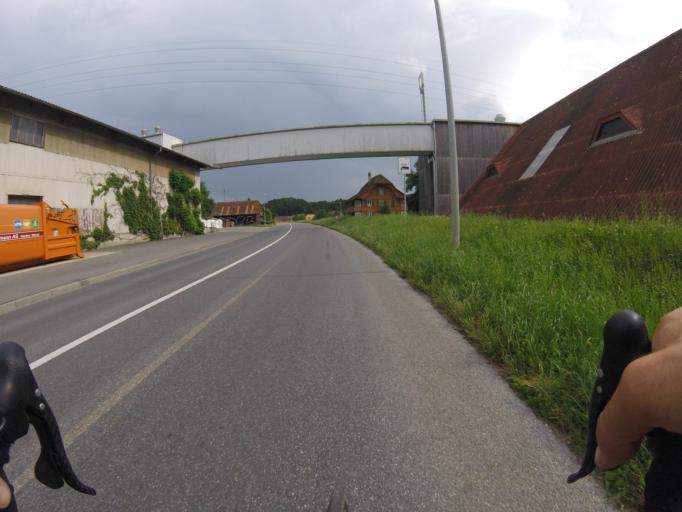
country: CH
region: Bern
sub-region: Seeland District
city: Grossaffoltern
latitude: 47.0562
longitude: 7.3395
